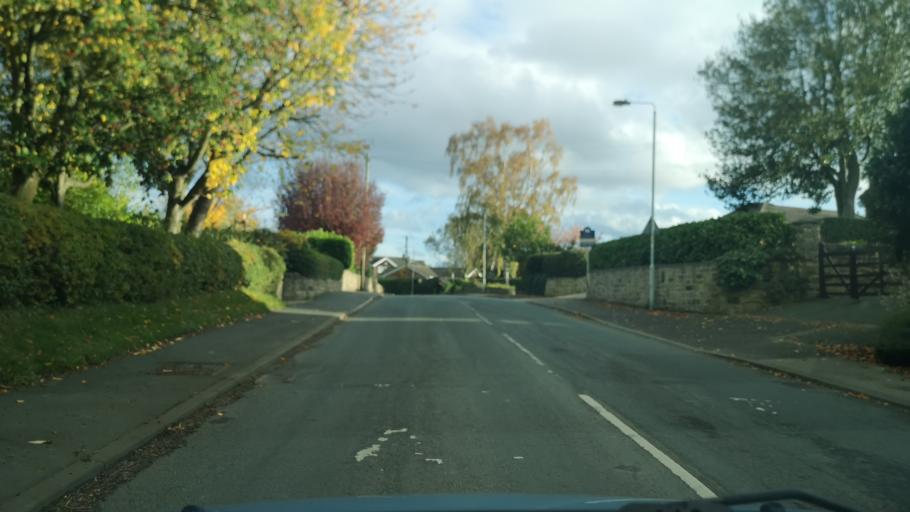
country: GB
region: England
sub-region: City and Borough of Wakefield
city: Notton
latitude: 53.6137
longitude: -1.4755
